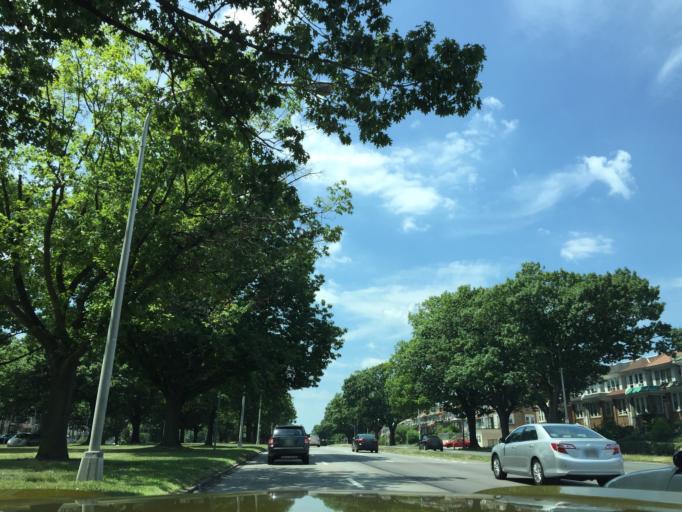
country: US
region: Pennsylvania
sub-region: Montgomery County
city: Rockledge
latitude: 40.0290
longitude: -75.1069
